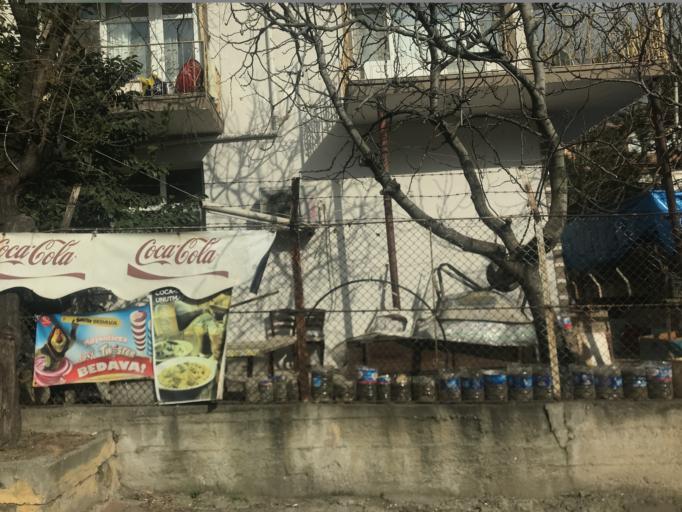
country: TR
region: Karabuk
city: Safranbolu
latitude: 41.2539
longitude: 32.6827
